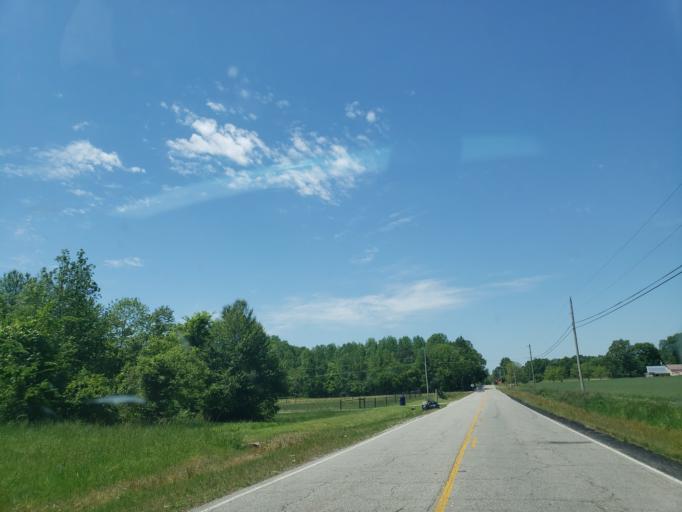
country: US
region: Alabama
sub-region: Madison County
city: Hazel Green
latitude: 34.9614
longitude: -86.5405
